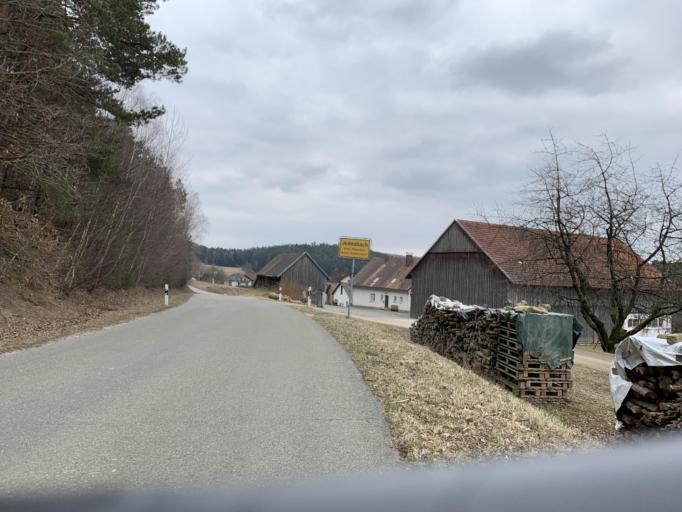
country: DE
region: Bavaria
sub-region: Upper Palatinate
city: Thanstein
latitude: 49.3706
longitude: 12.4366
